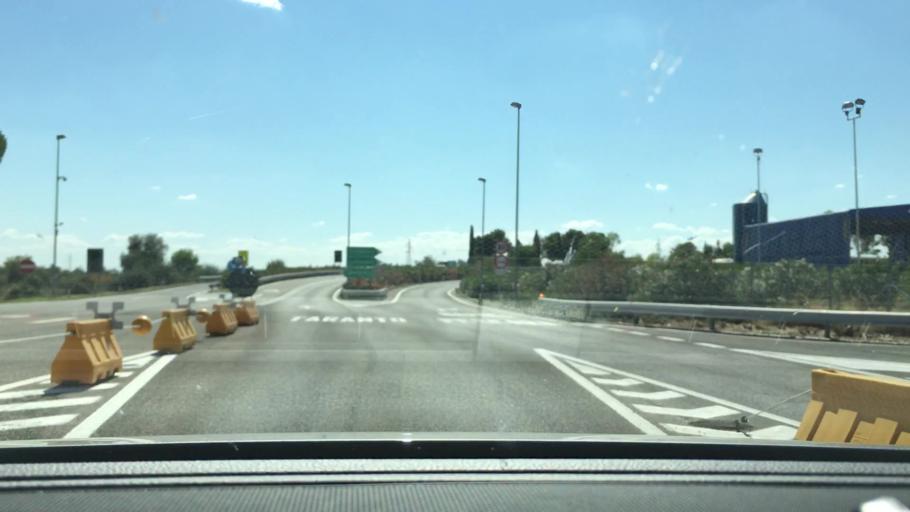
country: IT
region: Apulia
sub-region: Provincia di Bari
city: Bitritto
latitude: 41.0681
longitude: 16.8315
